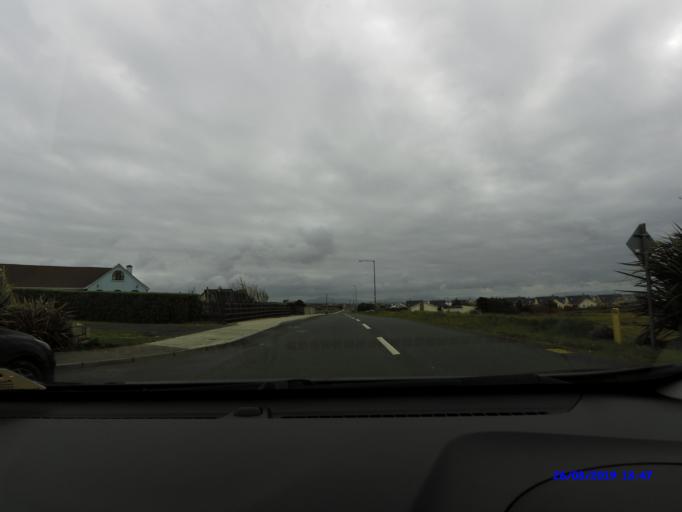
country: IE
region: Connaught
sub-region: Maigh Eo
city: Belmullet
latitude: 54.2183
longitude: -9.9834
